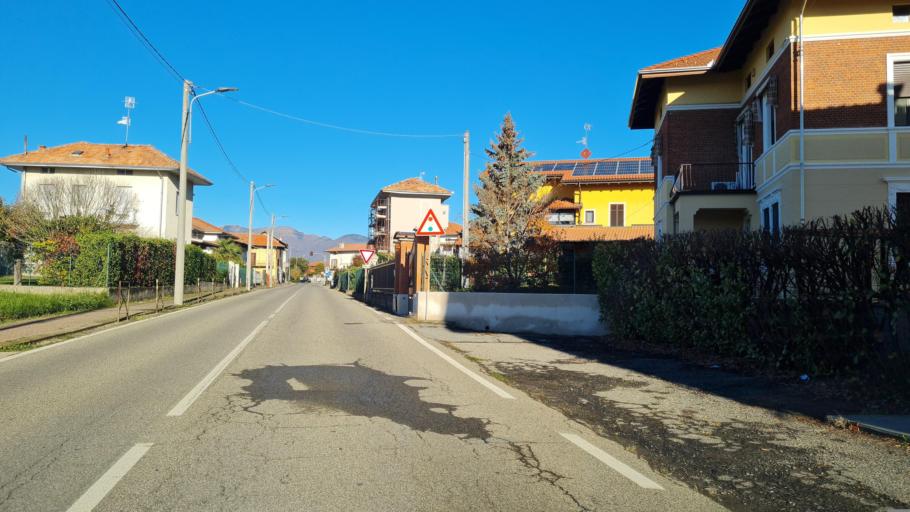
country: IT
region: Piedmont
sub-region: Provincia di Biella
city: Cossato
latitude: 45.5655
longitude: 8.1942
